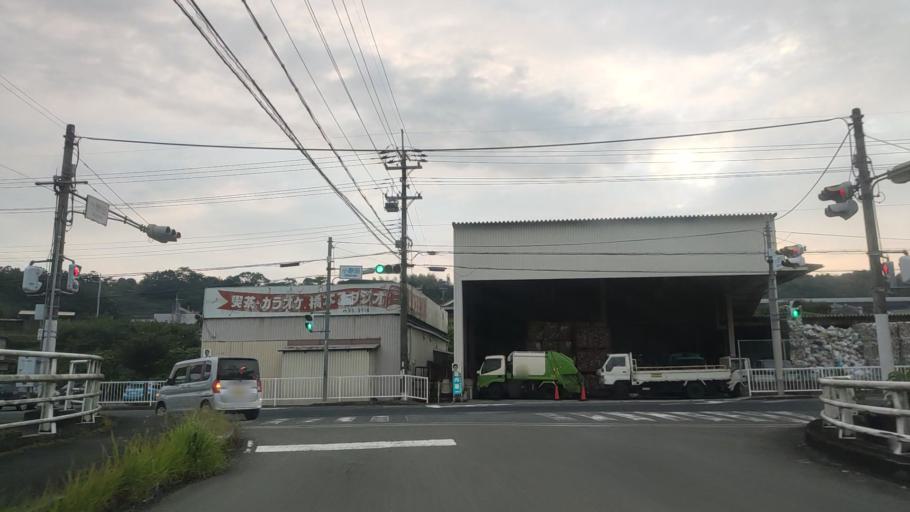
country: JP
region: Wakayama
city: Hashimoto
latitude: 34.3286
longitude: 135.6083
